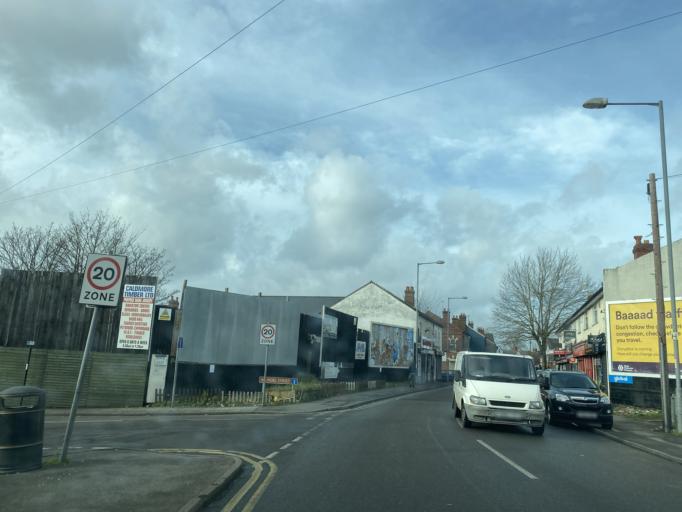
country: GB
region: England
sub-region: Walsall
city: Walsall
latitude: 52.5751
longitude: -1.9808
